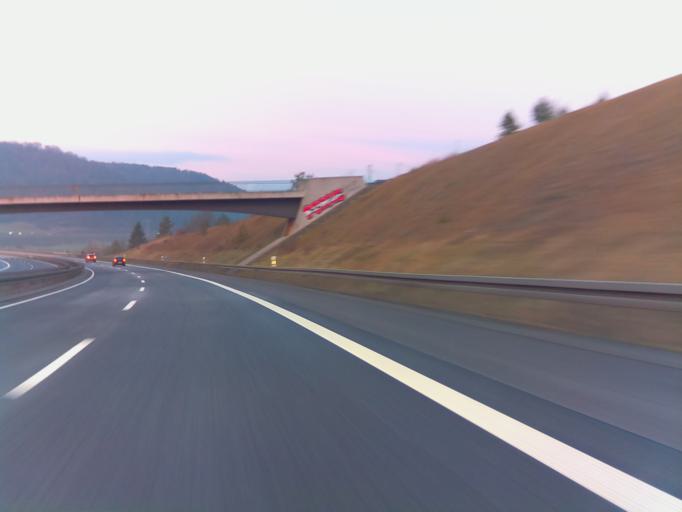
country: DE
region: Thuringia
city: Ellingshausen
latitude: 50.5463
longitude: 10.4794
